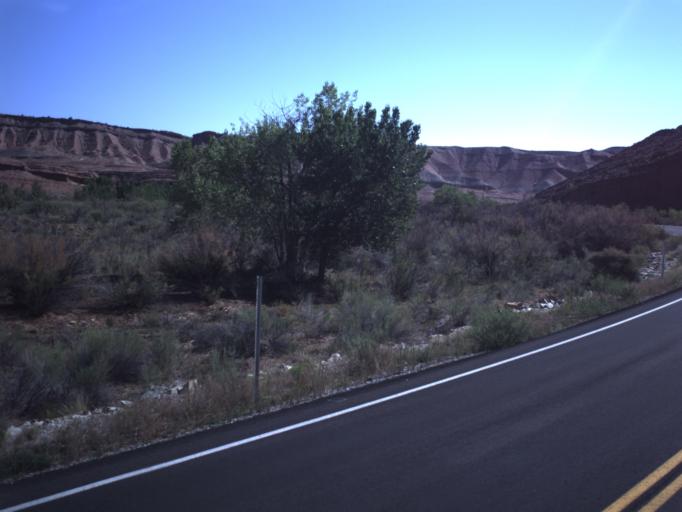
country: US
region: Utah
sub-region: Wayne County
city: Loa
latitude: 38.2842
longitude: -111.1481
